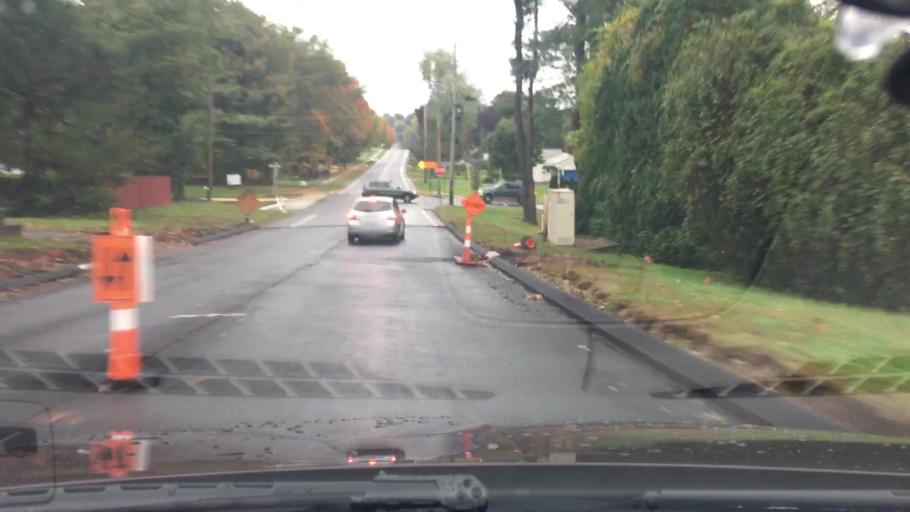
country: US
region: Connecticut
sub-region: Hartford County
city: Manchester
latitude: 41.8204
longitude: -72.5212
